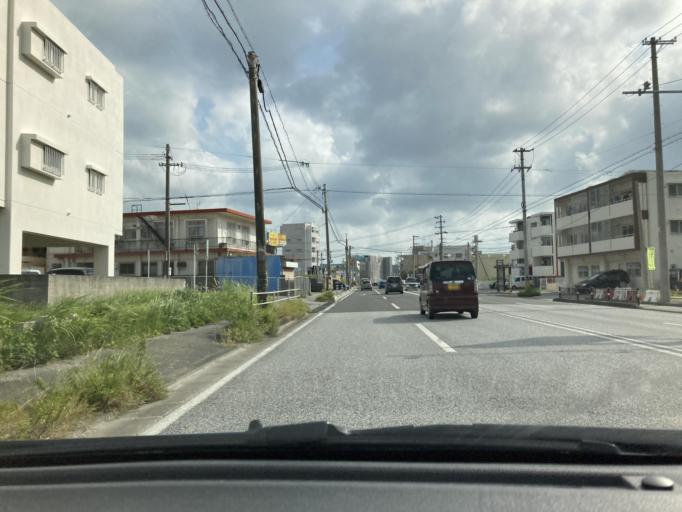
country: JP
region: Okinawa
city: Ginowan
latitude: 26.2228
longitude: 127.7657
